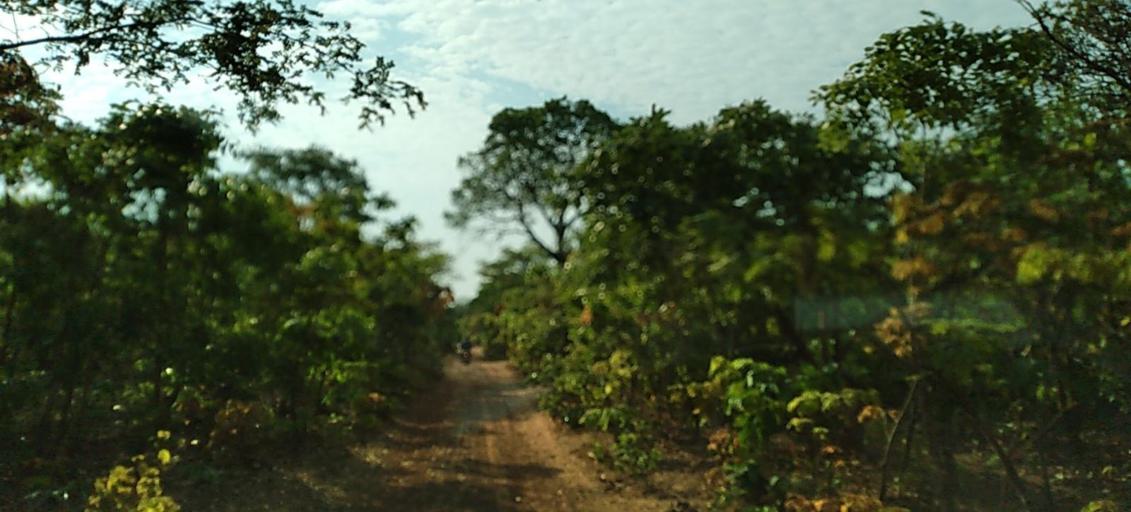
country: ZM
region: Copperbelt
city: Kalulushi
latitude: -12.9591
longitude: 27.6985
